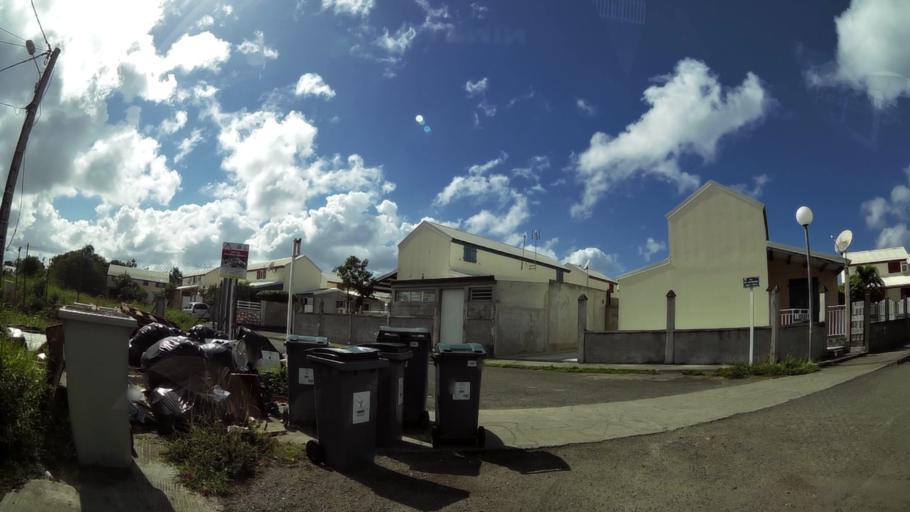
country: GP
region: Guadeloupe
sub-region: Guadeloupe
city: Port-Louis
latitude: 16.4210
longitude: -61.5287
